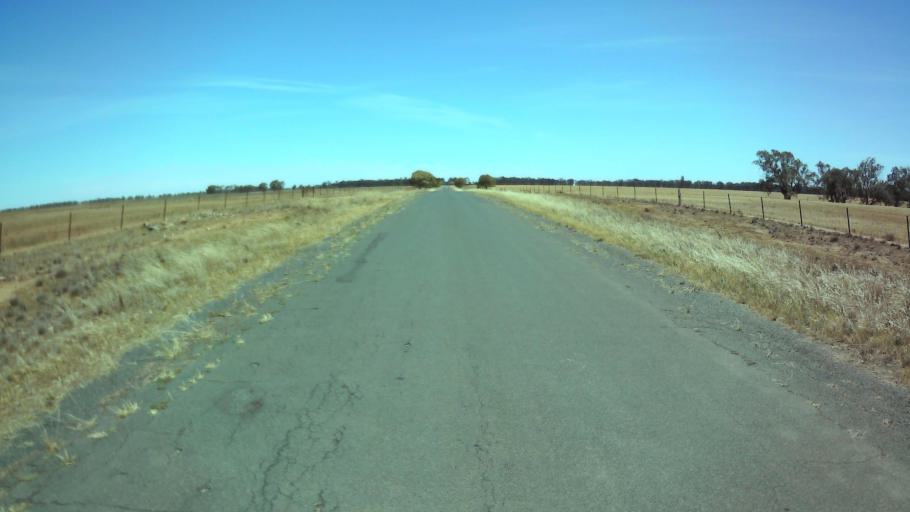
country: AU
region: New South Wales
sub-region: Weddin
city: Grenfell
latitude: -33.8504
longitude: 147.6957
